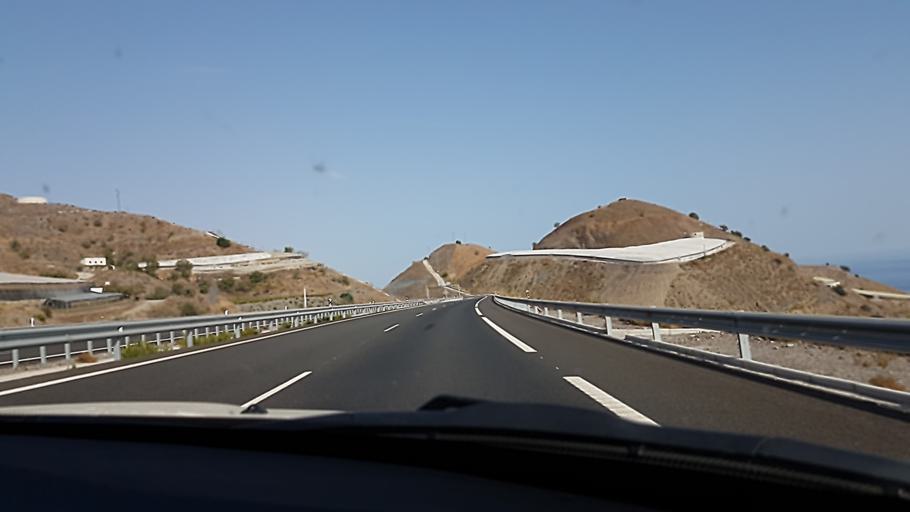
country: ES
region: Andalusia
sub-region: Provincia de Granada
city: Polopos
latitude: 36.7520
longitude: -3.2894
